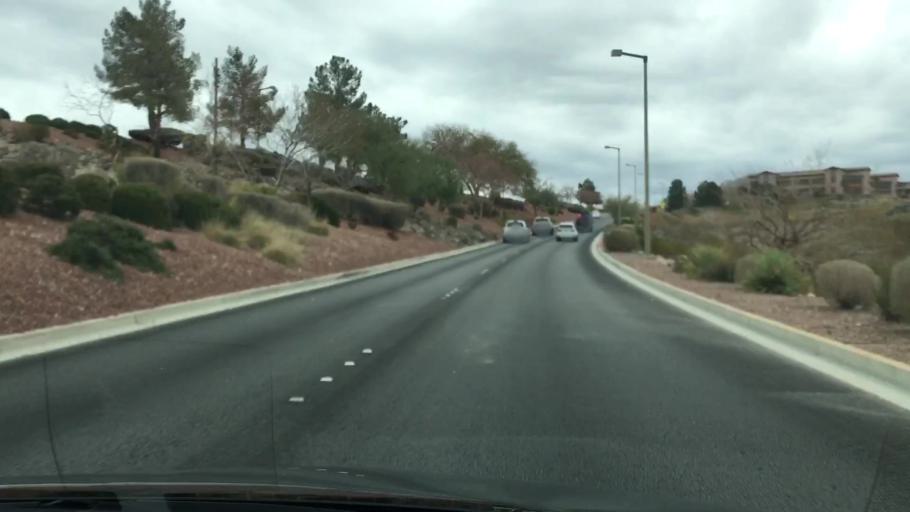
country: US
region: Nevada
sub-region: Clark County
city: Whitney
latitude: 35.9604
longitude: -115.0955
